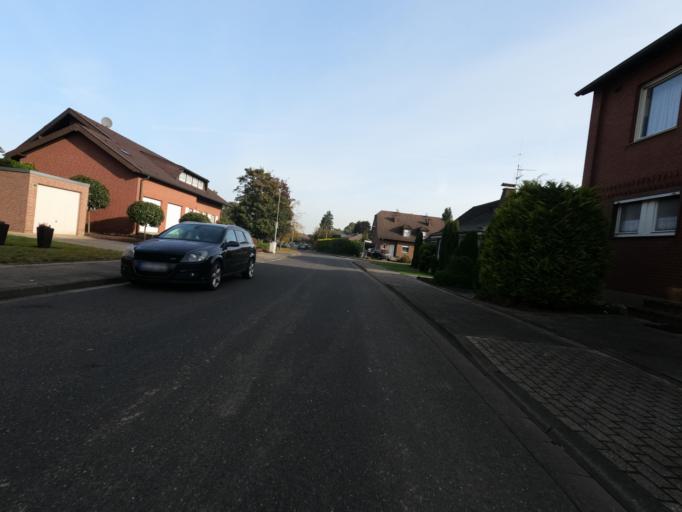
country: DE
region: North Rhine-Westphalia
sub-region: Regierungsbezirk Koln
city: Linnich
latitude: 50.9790
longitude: 6.2622
